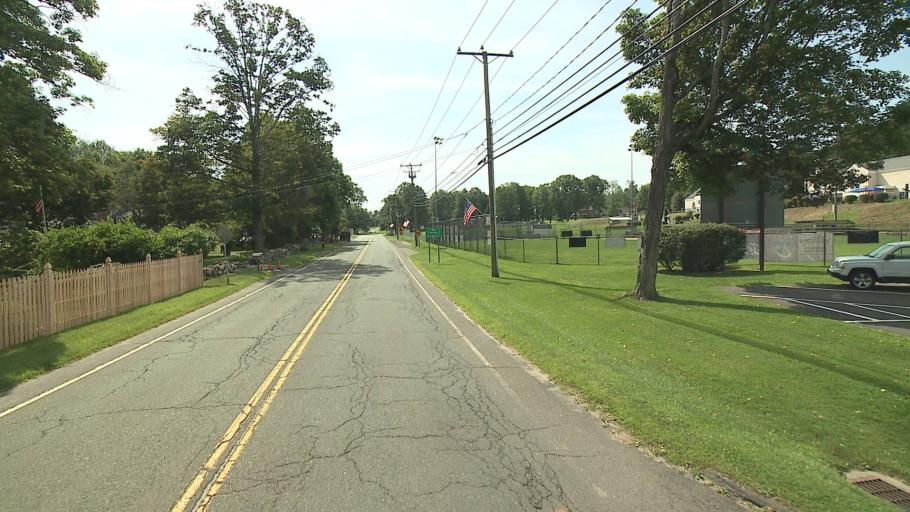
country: US
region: New York
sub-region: Putnam County
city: Putnam Lake
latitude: 41.4644
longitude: -73.4935
